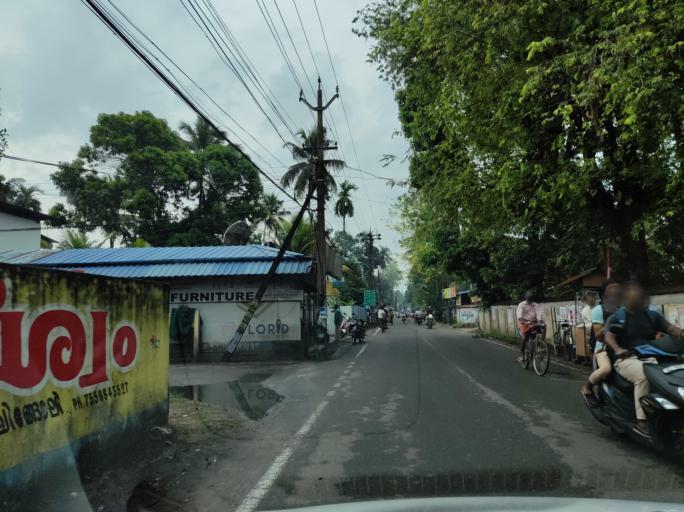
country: IN
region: Kerala
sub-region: Alappuzha
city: Kayankulam
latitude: 9.2406
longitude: 76.4543
